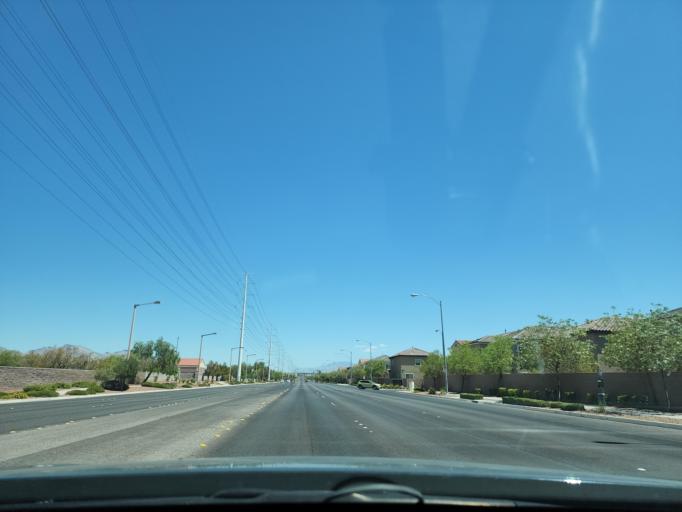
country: US
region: Nevada
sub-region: Clark County
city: Summerlin South
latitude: 36.0957
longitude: -115.3153
